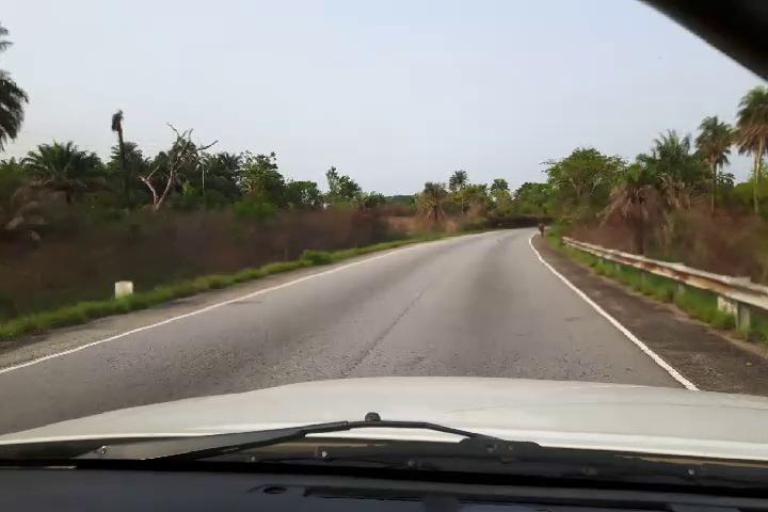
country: SL
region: Southern Province
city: Palima
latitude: 7.9320
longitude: -11.5270
